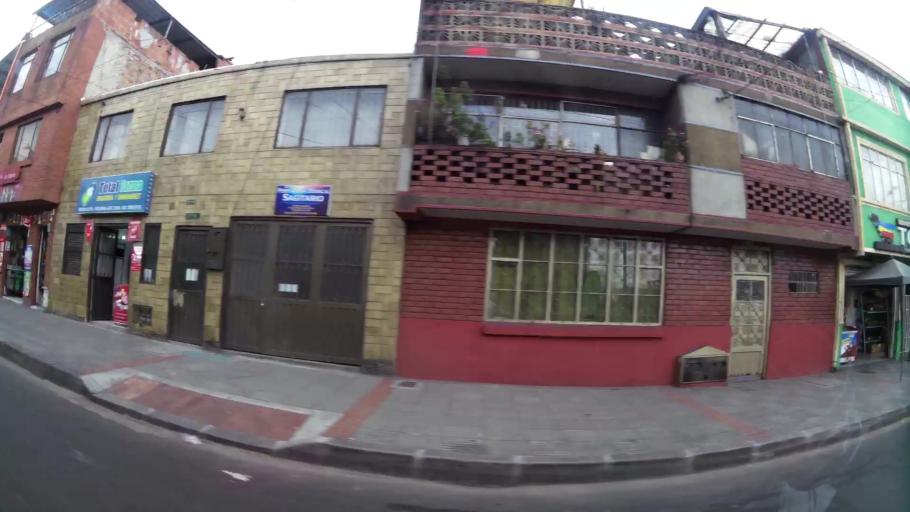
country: CO
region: Bogota D.C.
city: Bogota
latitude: 4.5734
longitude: -74.0939
